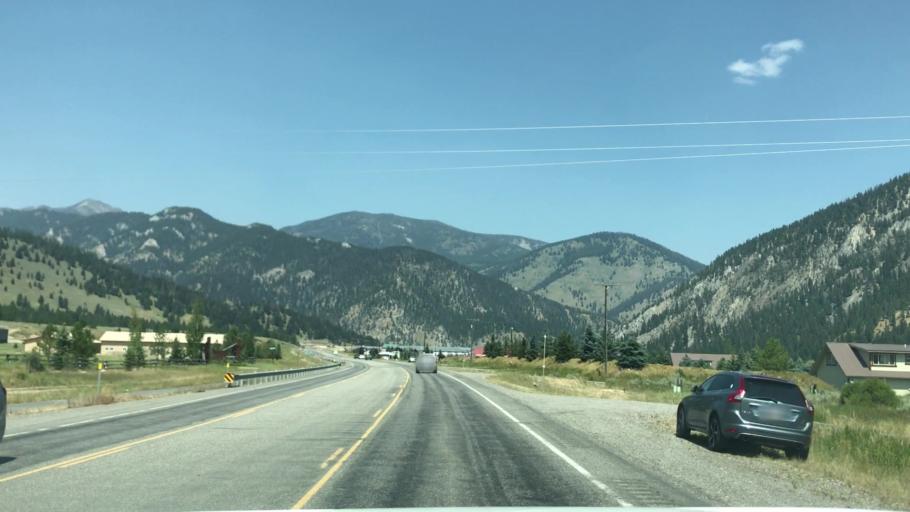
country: US
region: Montana
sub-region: Gallatin County
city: Big Sky
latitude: 45.2462
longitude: -111.2511
